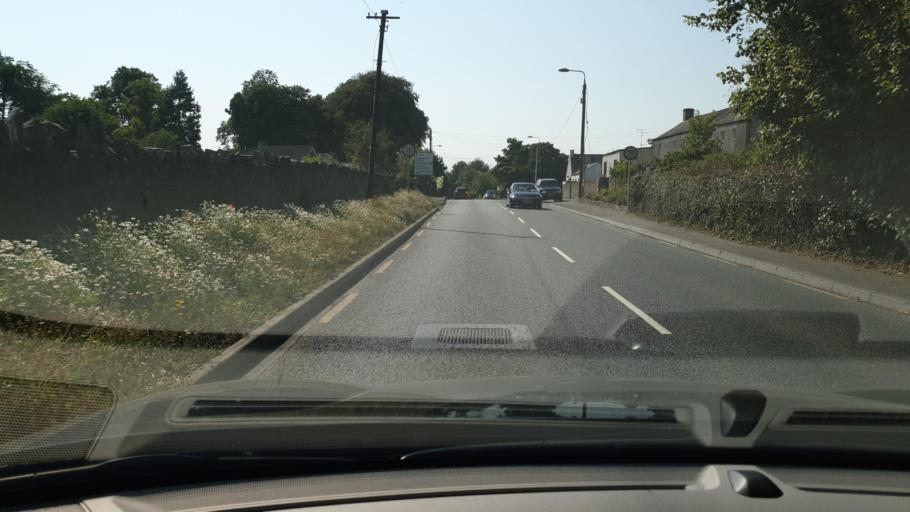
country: IE
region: Leinster
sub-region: An Mhi
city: Newtown Trim
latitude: 53.4803
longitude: -6.7296
